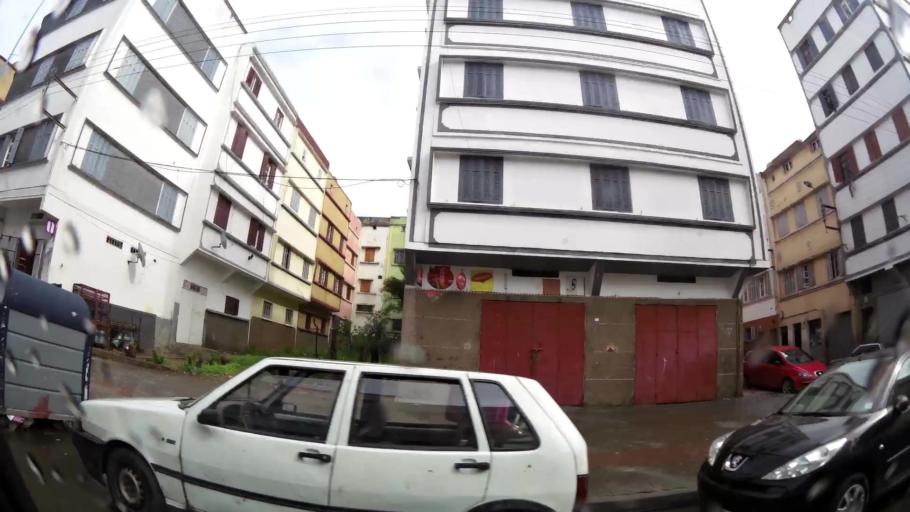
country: MA
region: Grand Casablanca
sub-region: Casablanca
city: Casablanca
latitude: 33.5432
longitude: -7.5745
